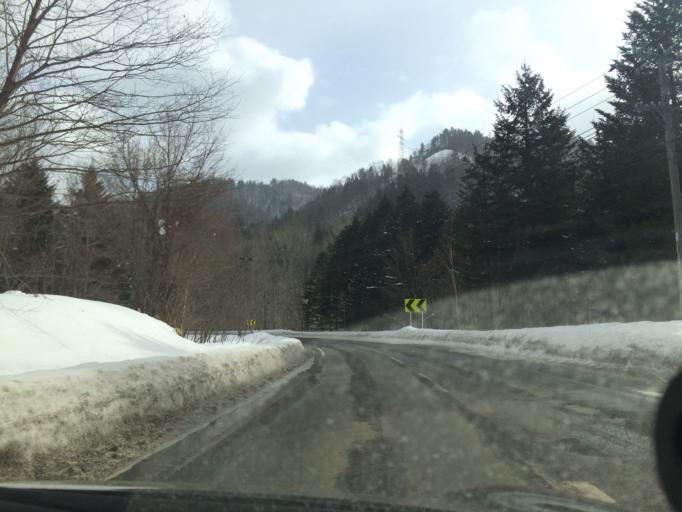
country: JP
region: Hokkaido
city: Shimo-furano
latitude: 43.0511
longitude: 142.4974
